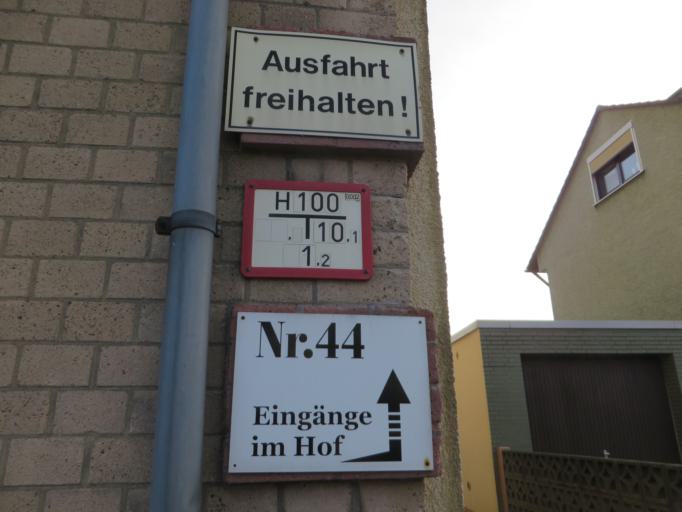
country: DE
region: North Rhine-Westphalia
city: Witten
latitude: 51.4817
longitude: 7.3493
